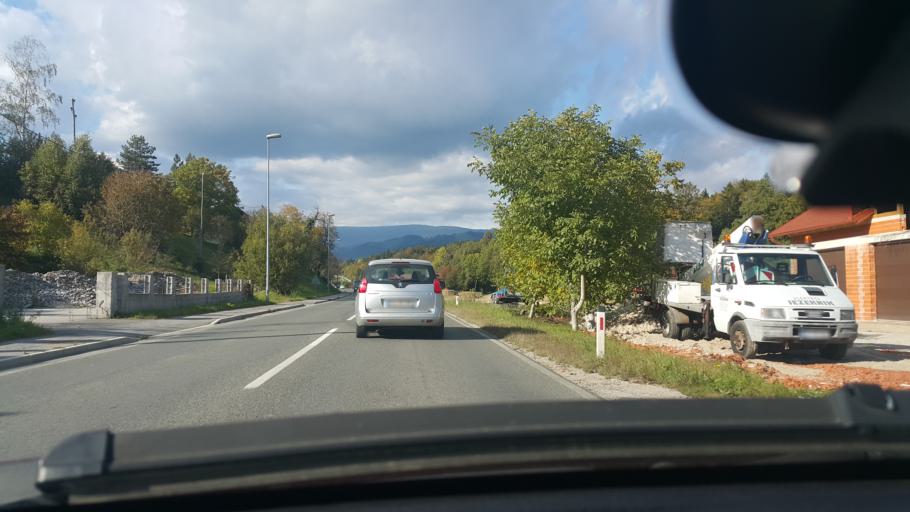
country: SI
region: Slovenska Konjice
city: Slovenske Konjice
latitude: 46.3529
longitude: 15.4006
